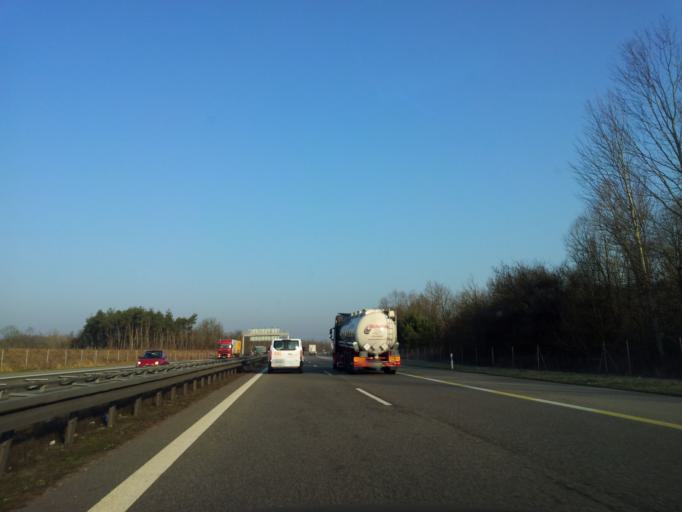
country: FR
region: Alsace
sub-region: Departement du Haut-Rhin
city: Rosenau
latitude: 47.6525
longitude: 7.5372
